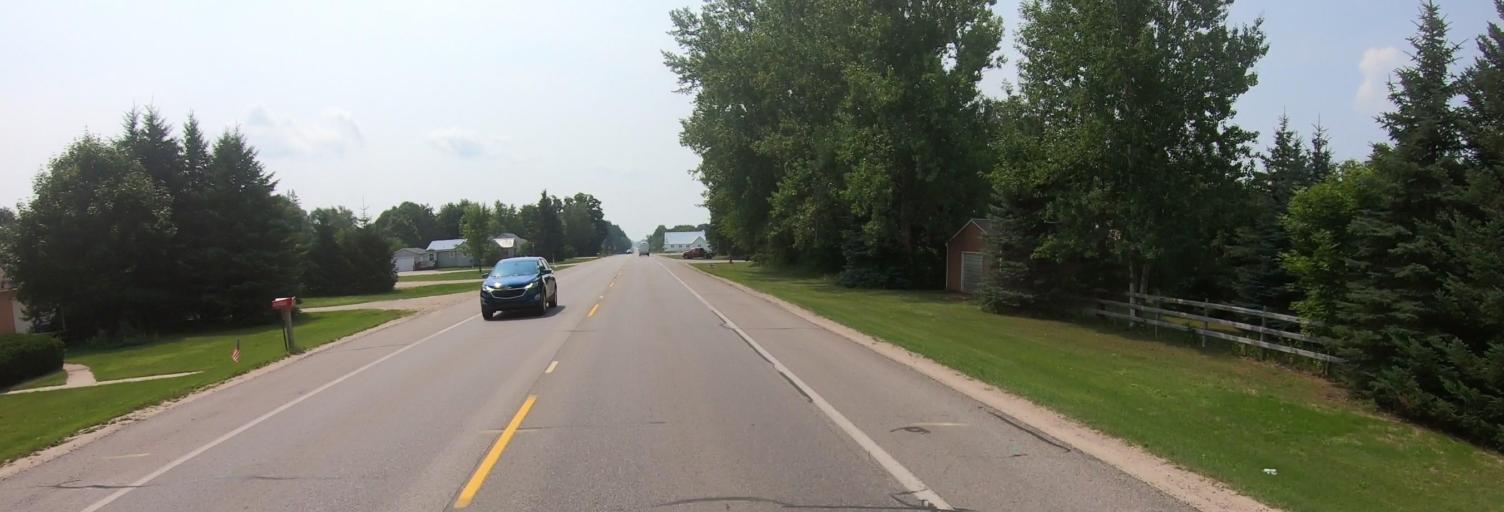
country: US
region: Michigan
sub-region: Luce County
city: Newberry
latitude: 46.3284
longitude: -85.5098
